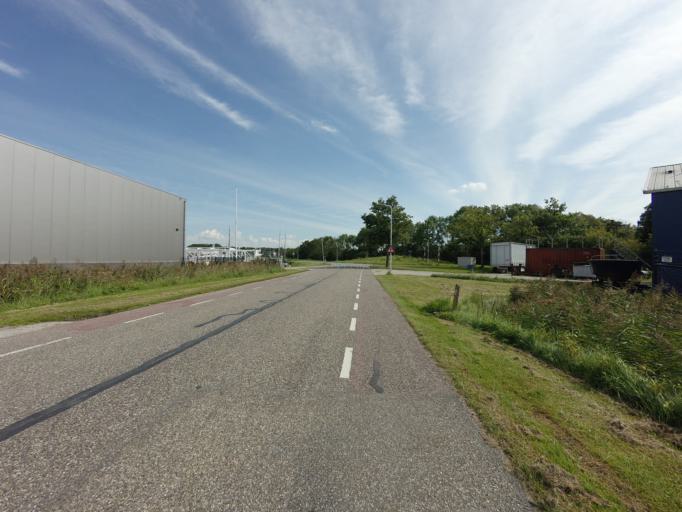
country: NL
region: Friesland
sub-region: Gemeente Harlingen
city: Harlingen
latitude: 53.1735
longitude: 5.4532
